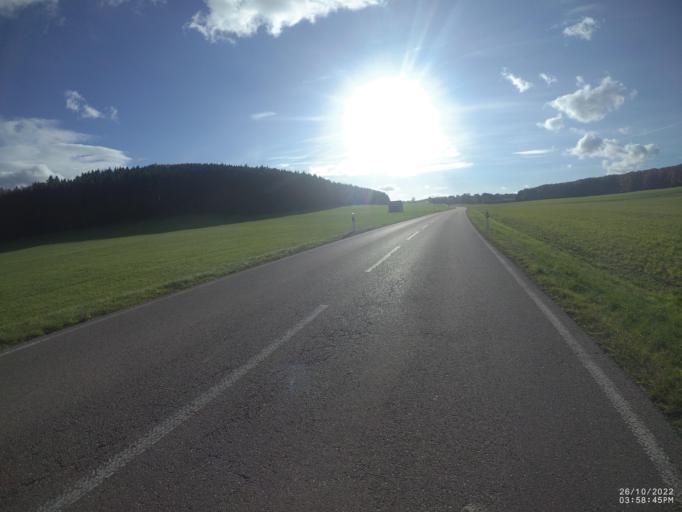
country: DE
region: Baden-Wuerttemberg
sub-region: Regierungsbezirk Stuttgart
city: Hohenstadt
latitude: 48.5258
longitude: 9.6556
